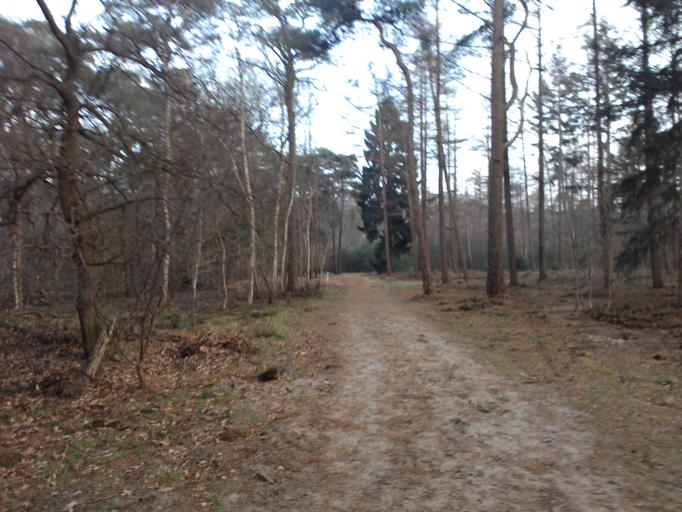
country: NL
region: Utrecht
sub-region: Gemeente Zeist
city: Zeist
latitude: 52.1099
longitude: 5.2112
